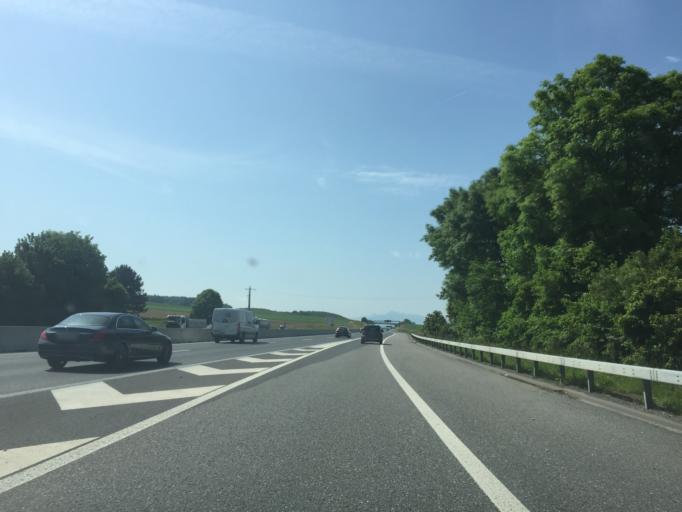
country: CH
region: Vaud
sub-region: Gros-de-Vaud District
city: Penthalaz
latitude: 46.5956
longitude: 6.5535
